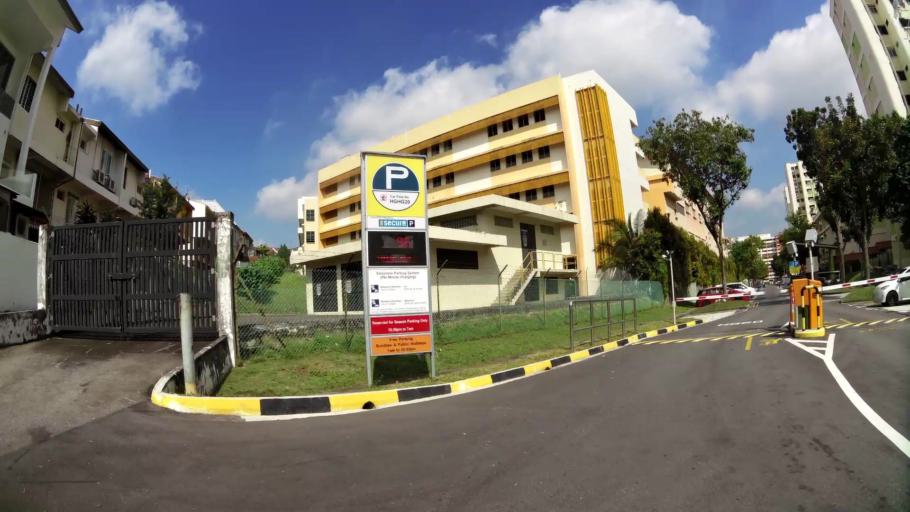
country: SG
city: Singapore
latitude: 1.3489
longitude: 103.8862
